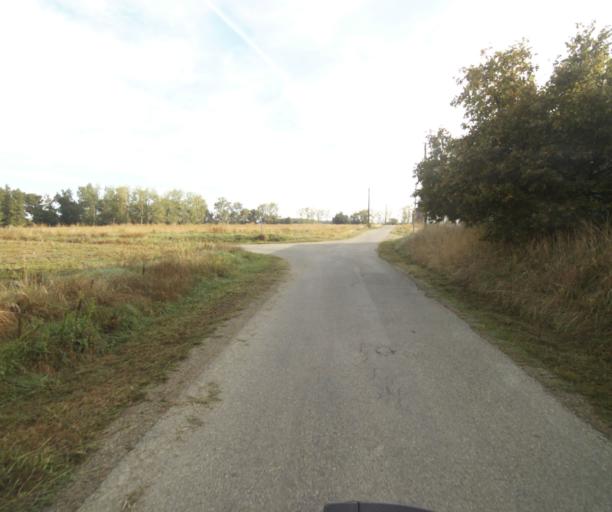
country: FR
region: Midi-Pyrenees
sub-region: Departement du Tarn-et-Garonne
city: Montech
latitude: 43.9744
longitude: 1.2250
